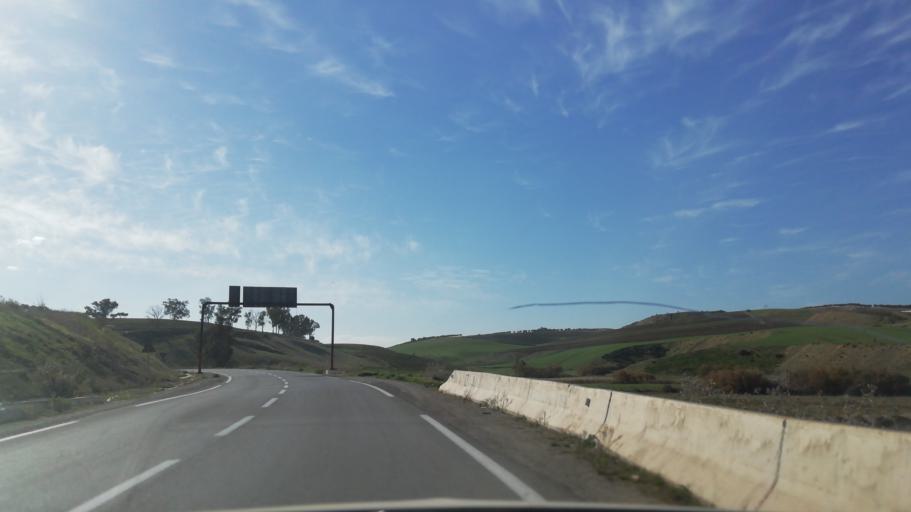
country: DZ
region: Tlemcen
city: Chetouane
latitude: 34.9803
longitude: -1.2380
